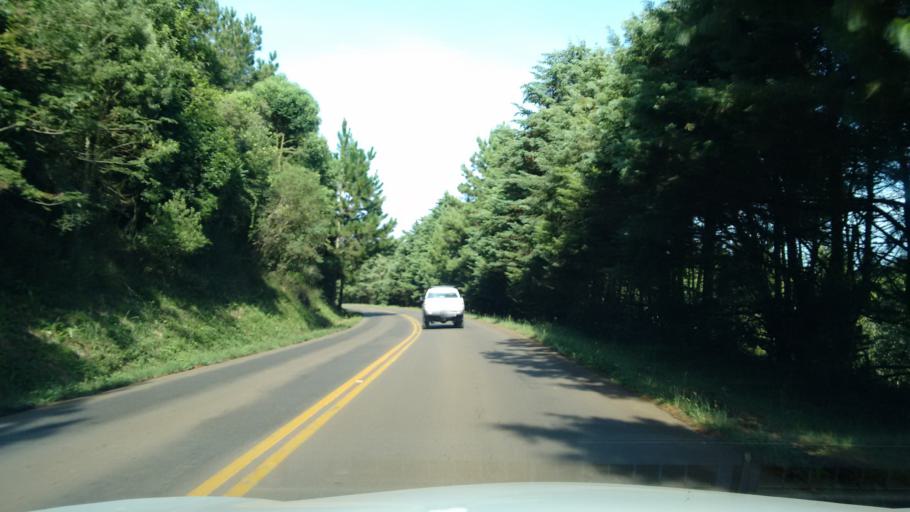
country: BR
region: Santa Catarina
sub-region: Videira
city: Videira
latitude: -27.1328
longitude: -50.9423
